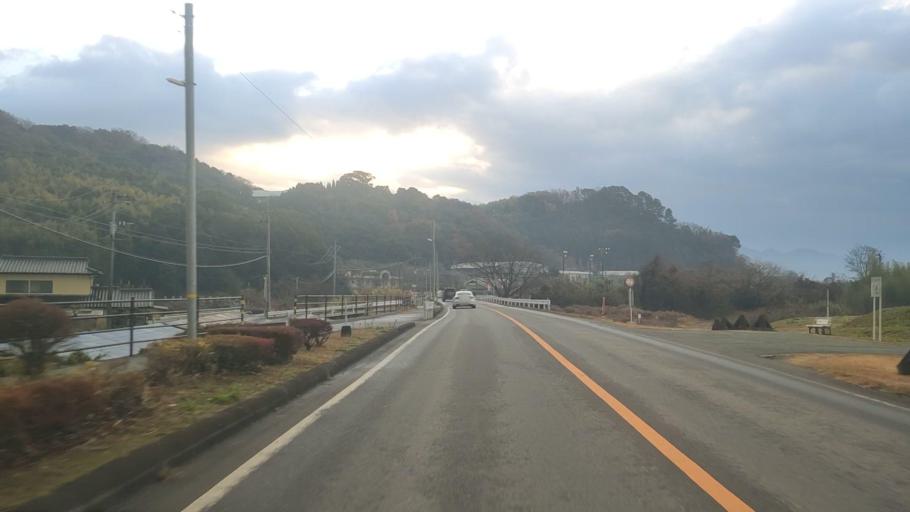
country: JP
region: Kumamoto
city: Uto
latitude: 32.6995
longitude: 130.7846
